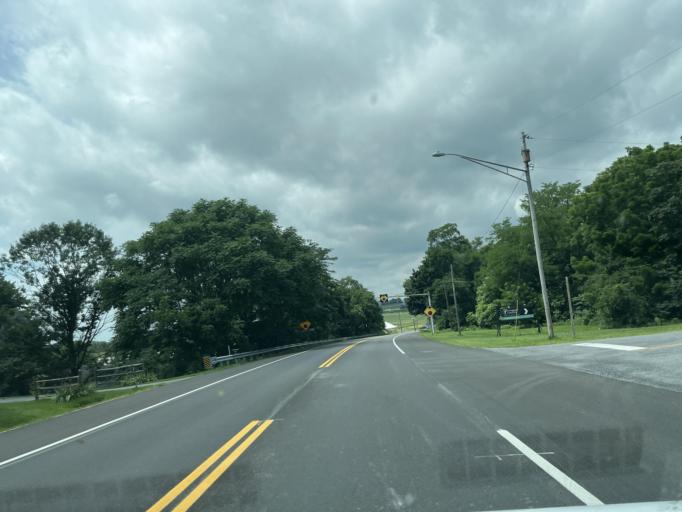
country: US
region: Pennsylvania
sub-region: Franklin County
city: Wayne Heights
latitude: 39.7079
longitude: -77.5687
